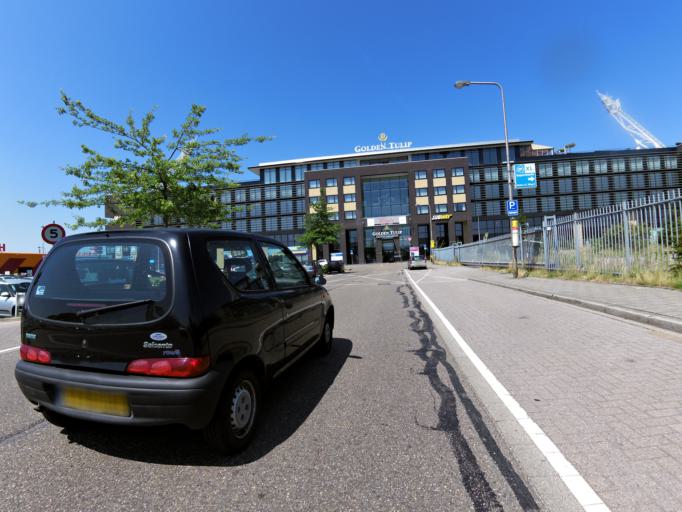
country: NL
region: Limburg
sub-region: Gemeente Simpelveld
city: Simpelveld
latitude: 50.8558
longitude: 6.0068
